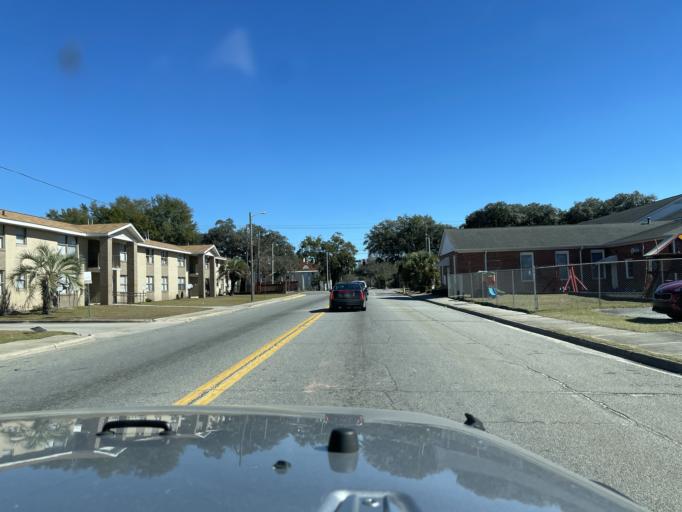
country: US
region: Georgia
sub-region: Chatham County
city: Savannah
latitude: 32.0641
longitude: -81.1045
